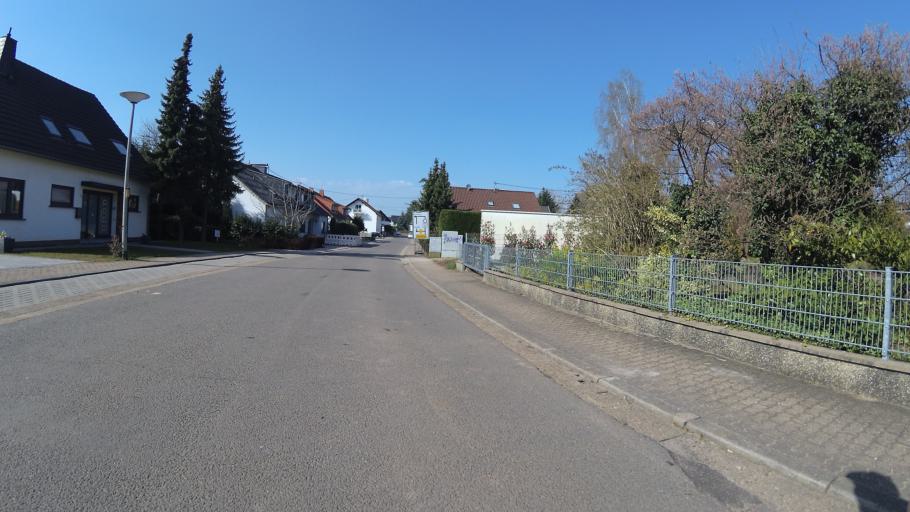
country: DE
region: Saarland
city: Heusweiler
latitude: 49.3292
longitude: 6.9852
